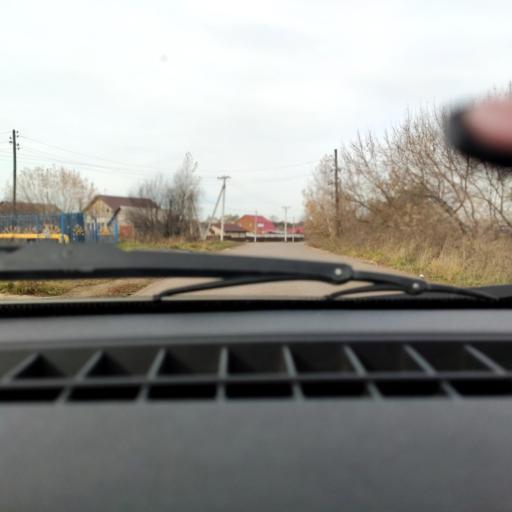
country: RU
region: Bashkortostan
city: Iglino
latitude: 54.8139
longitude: 56.1904
